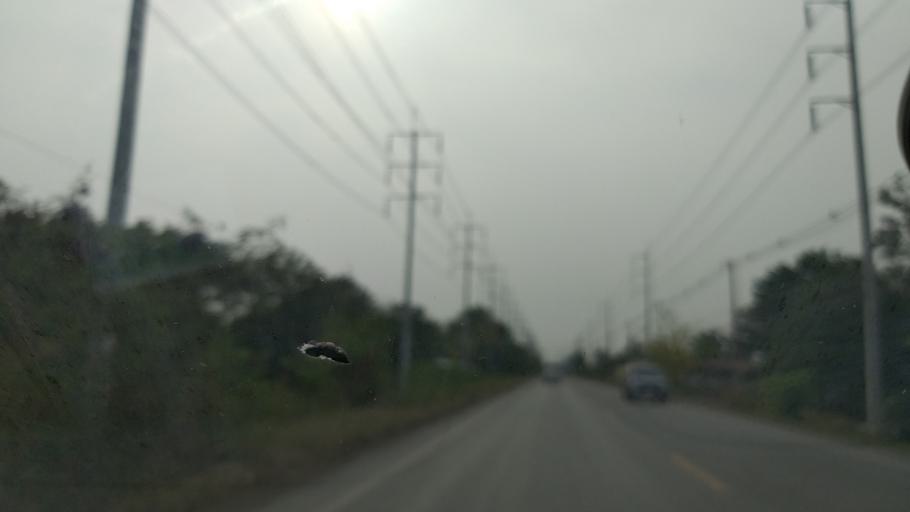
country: TH
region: Chachoengsao
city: Ban Pho
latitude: 13.6041
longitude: 101.1355
